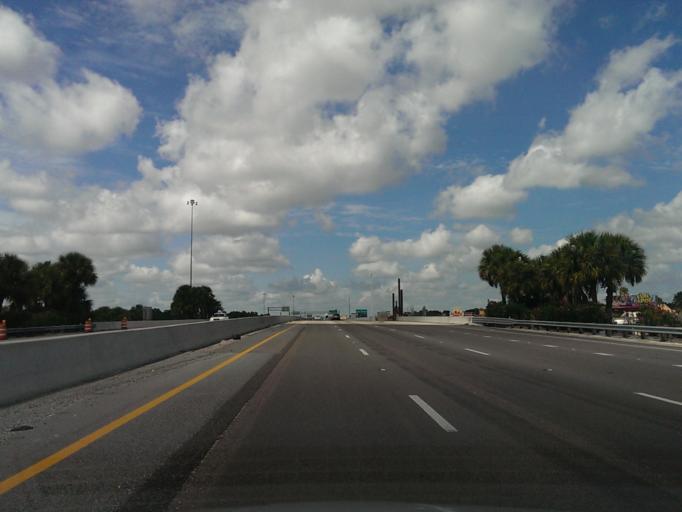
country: US
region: Florida
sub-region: Orange County
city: Belle Isle
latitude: 28.4513
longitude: -81.3323
